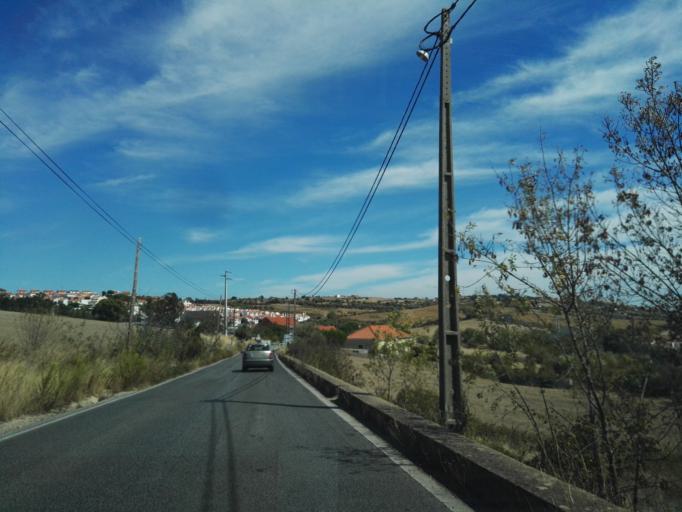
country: PT
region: Lisbon
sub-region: Vila Franca de Xira
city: Sao Joao dos Montes
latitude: 38.9481
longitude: -9.0460
